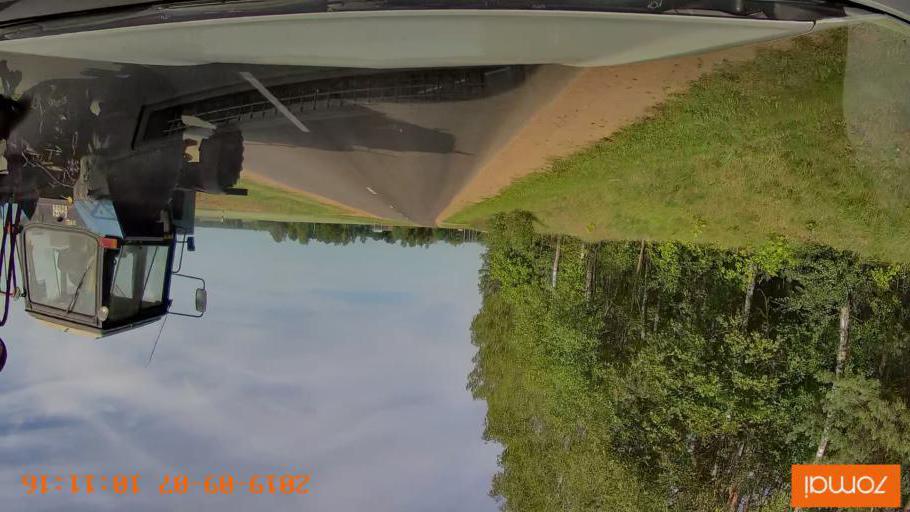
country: BY
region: Grodnenskaya
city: Voranava
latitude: 54.1207
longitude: 25.3672
